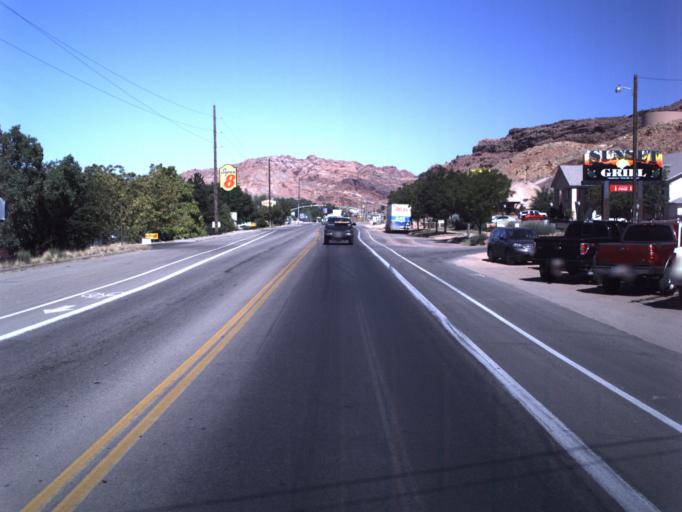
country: US
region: Utah
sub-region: Grand County
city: Moab
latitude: 38.5866
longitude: -109.5581
